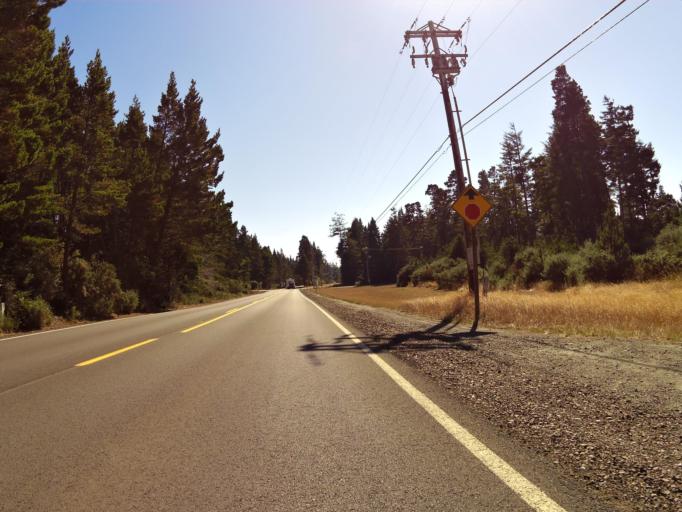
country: US
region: Oregon
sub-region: Coos County
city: Bandon
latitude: 43.1885
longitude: -124.3677
